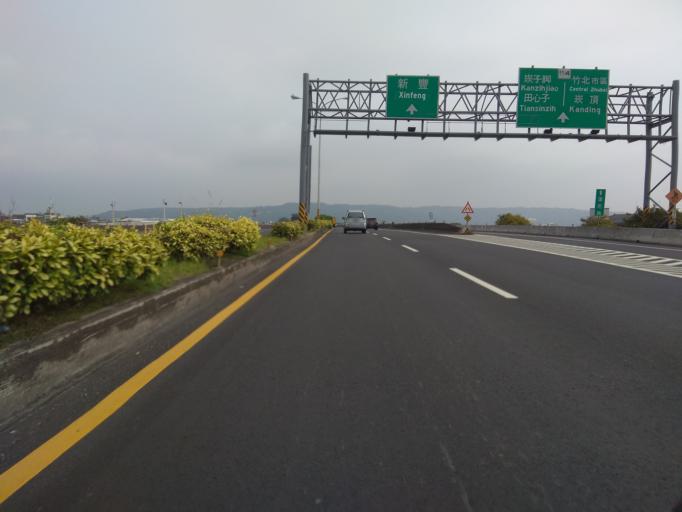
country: TW
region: Taiwan
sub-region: Hsinchu
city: Hsinchu
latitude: 24.8570
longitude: 120.9477
